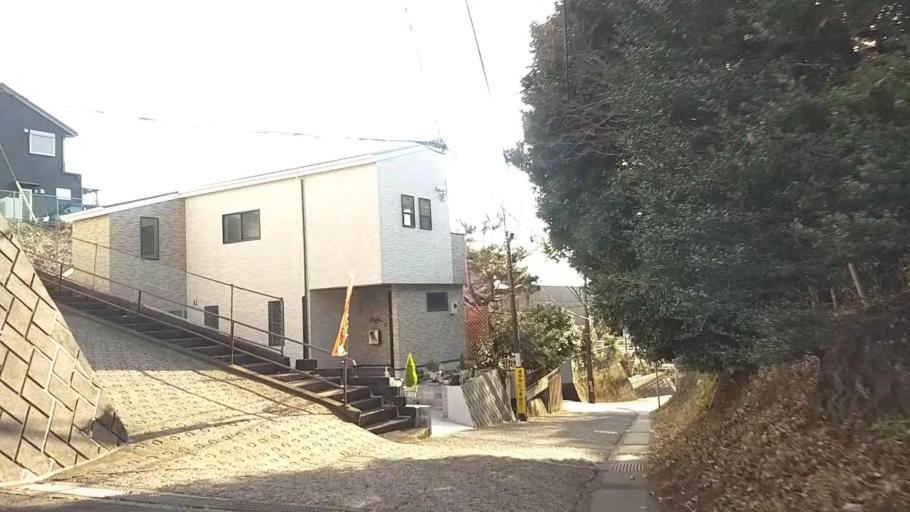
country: JP
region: Kanagawa
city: Atsugi
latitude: 35.4465
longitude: 139.3358
